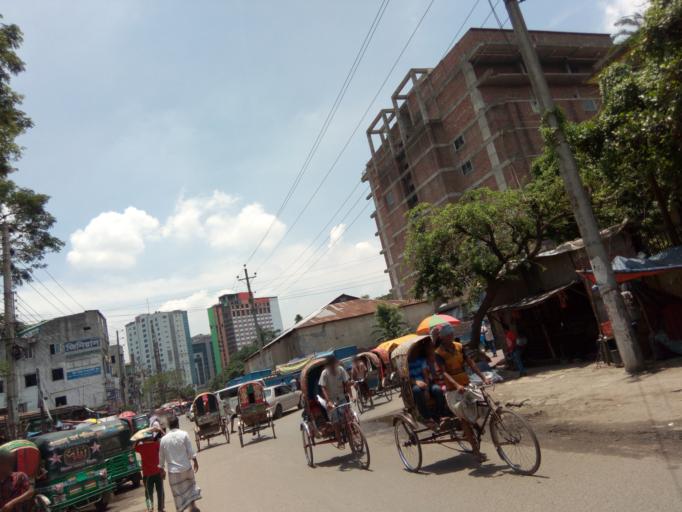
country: BD
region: Dhaka
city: Paltan
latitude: 23.7572
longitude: 90.4011
